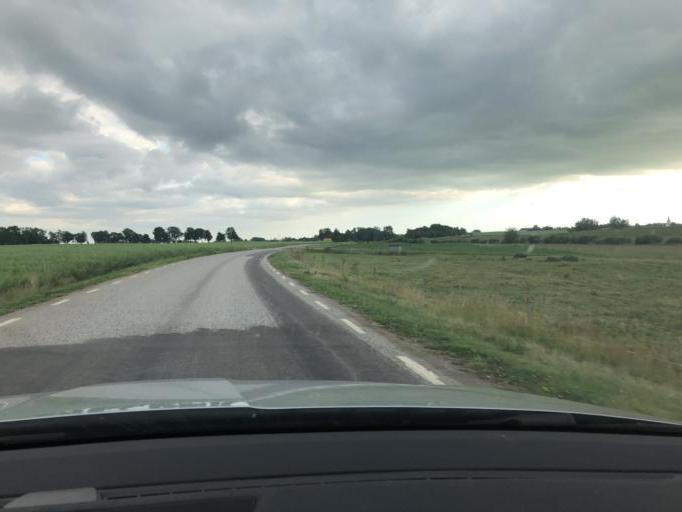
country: SE
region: Skane
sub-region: Simrishamns Kommun
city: Simrishamn
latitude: 55.5065
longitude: 14.2260
